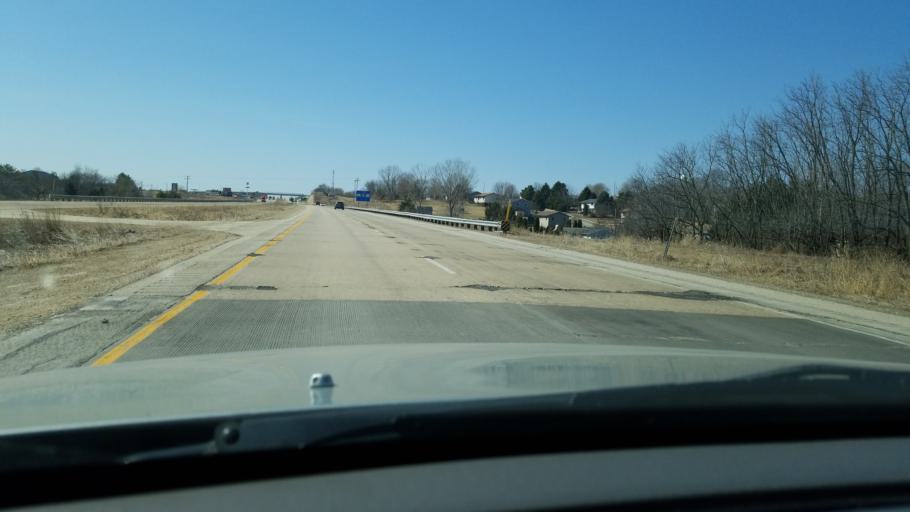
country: US
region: Wisconsin
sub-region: Iowa County
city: Barneveld
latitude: 43.0107
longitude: -89.8869
